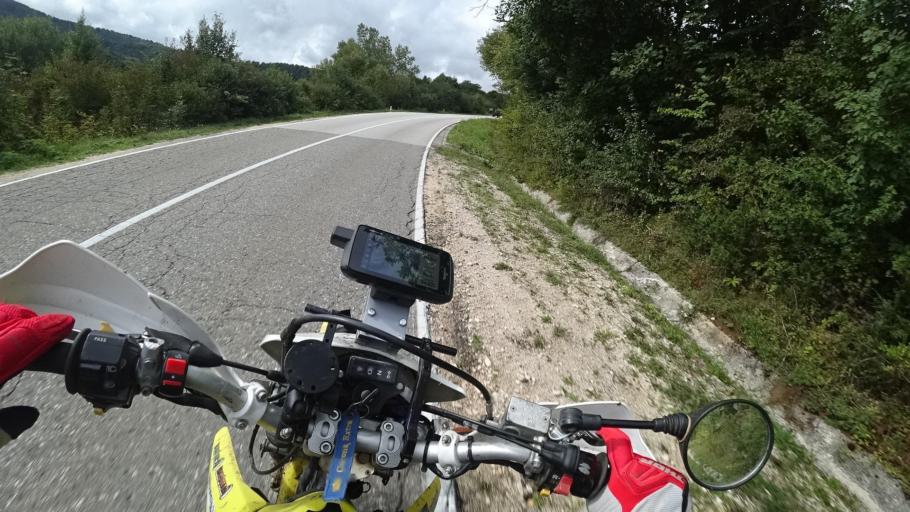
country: BA
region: Republika Srpska
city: Bronzani Majdan
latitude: 44.6547
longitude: 17.0232
